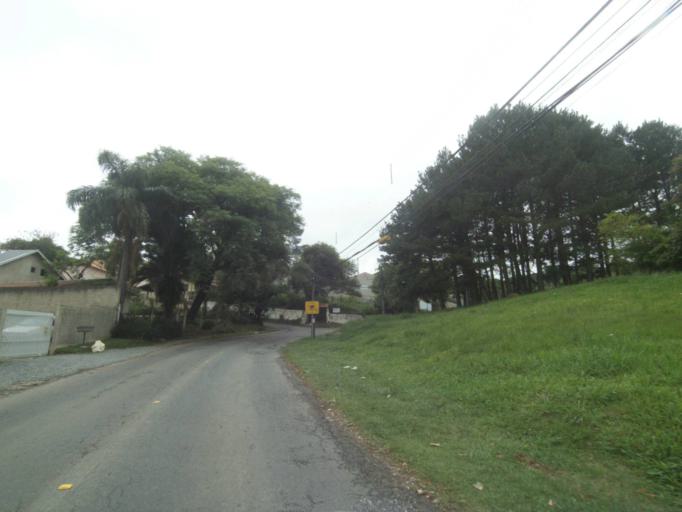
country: BR
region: Parana
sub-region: Curitiba
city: Curitiba
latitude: -25.4235
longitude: -49.3394
